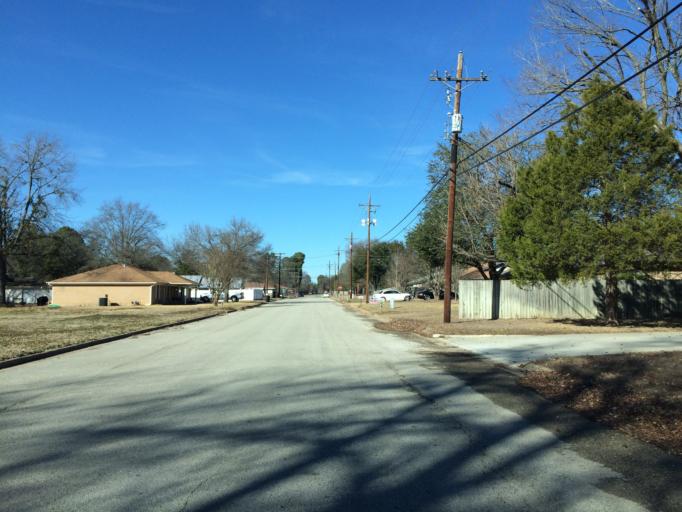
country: US
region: Texas
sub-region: Wood County
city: Mineola
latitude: 32.6787
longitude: -95.4824
